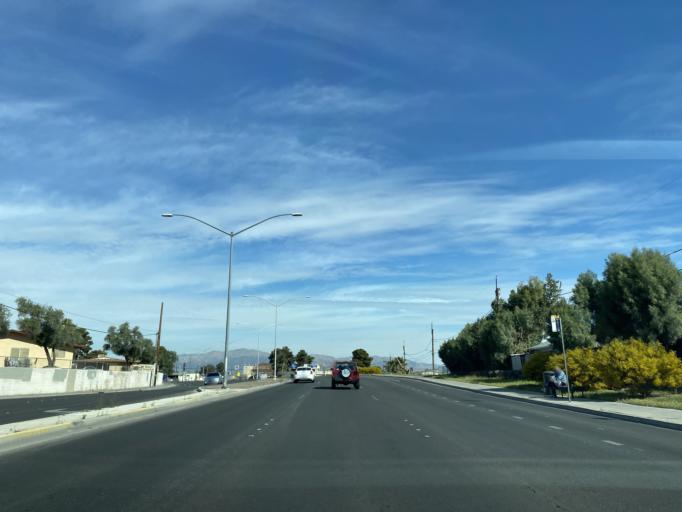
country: US
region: Nevada
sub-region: Clark County
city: Las Vegas
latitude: 36.1711
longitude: -115.1298
